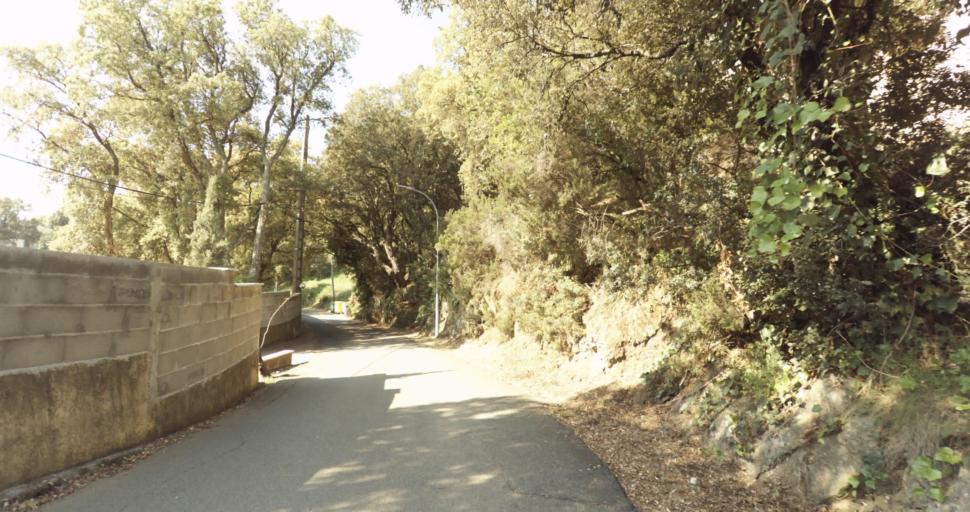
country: FR
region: Corsica
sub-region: Departement de la Haute-Corse
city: Biguglia
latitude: 42.6311
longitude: 9.4179
